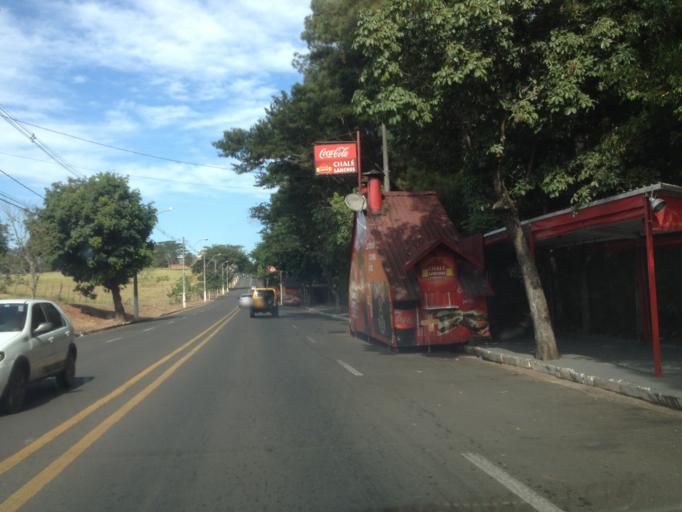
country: BR
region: Sao Paulo
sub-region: Marilia
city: Marilia
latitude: -22.2013
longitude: -49.9312
